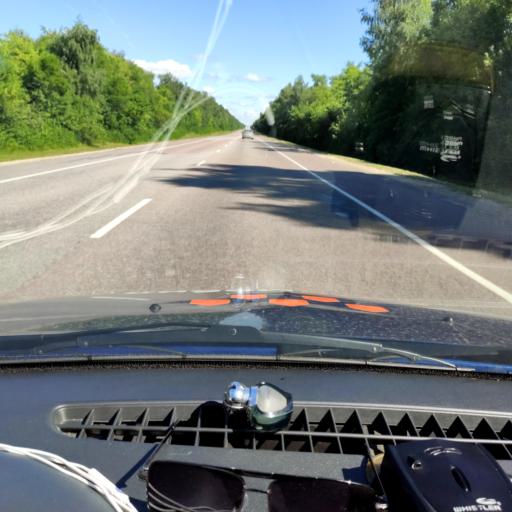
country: RU
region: Lipetsk
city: Khlevnoye
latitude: 52.2800
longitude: 39.1680
